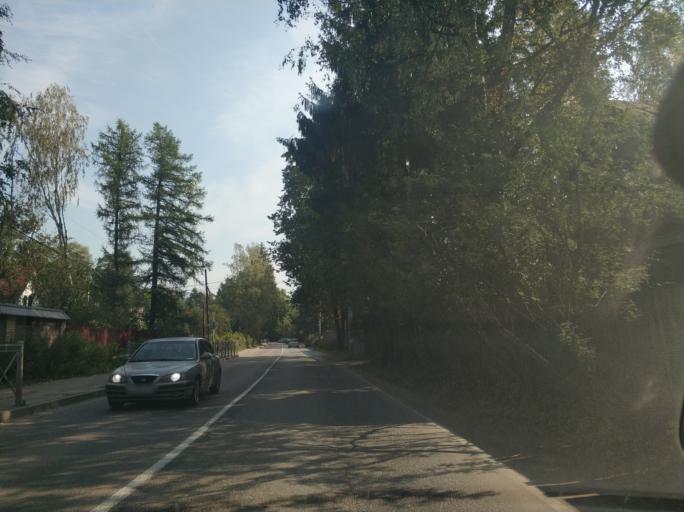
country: RU
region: Leningrad
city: Vsevolozhsk
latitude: 60.0092
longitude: 30.5990
